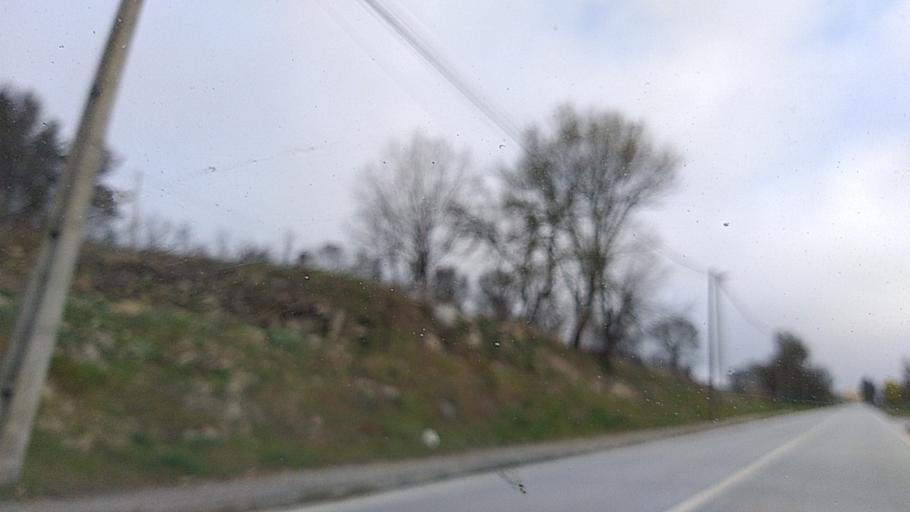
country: PT
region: Guarda
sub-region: Fornos de Algodres
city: Fornos de Algodres
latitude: 40.6784
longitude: -7.4725
